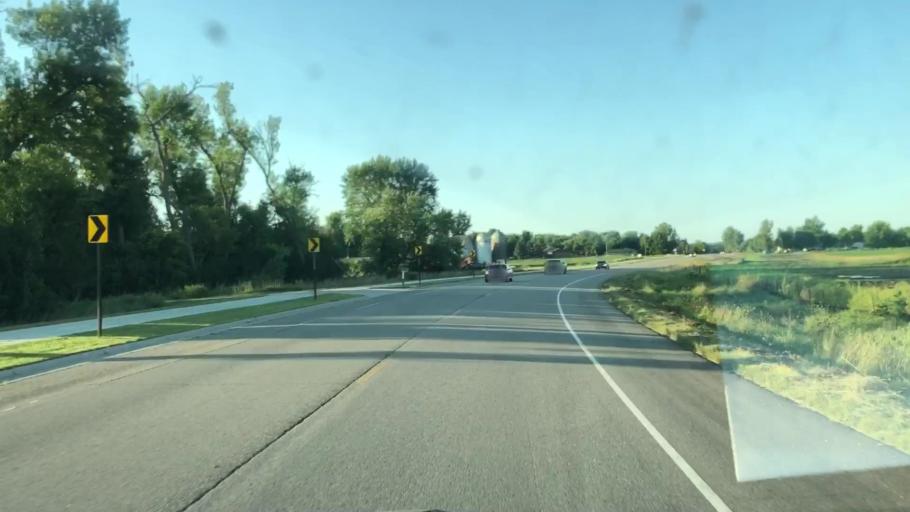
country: US
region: Minnesota
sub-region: Nobles County
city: Worthington
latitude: 43.6206
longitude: -95.6336
